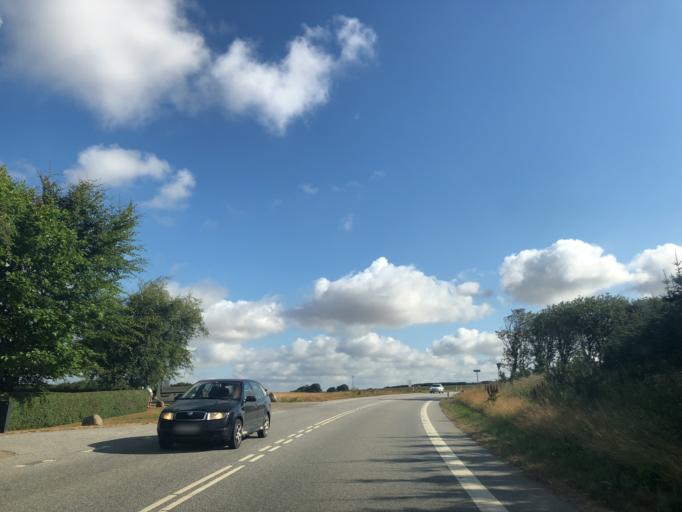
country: DK
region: Central Jutland
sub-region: Skive Kommune
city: Skive
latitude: 56.6251
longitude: 8.8833
